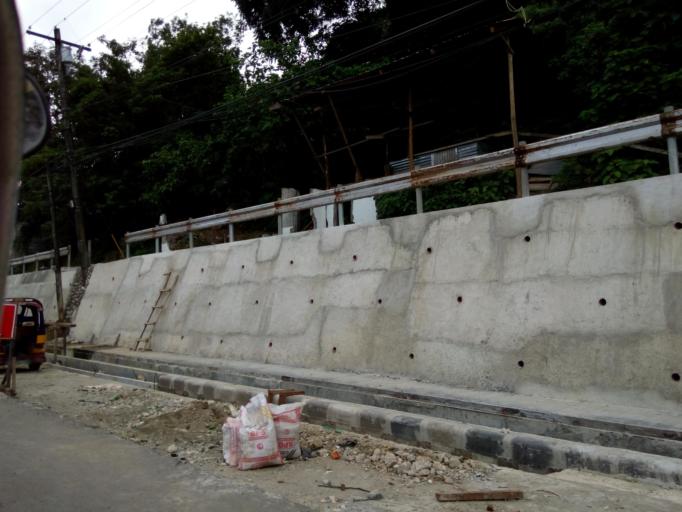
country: PH
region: Caraga
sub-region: Province of Surigao del Norte
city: Surigao
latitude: 9.7840
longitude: 125.4882
